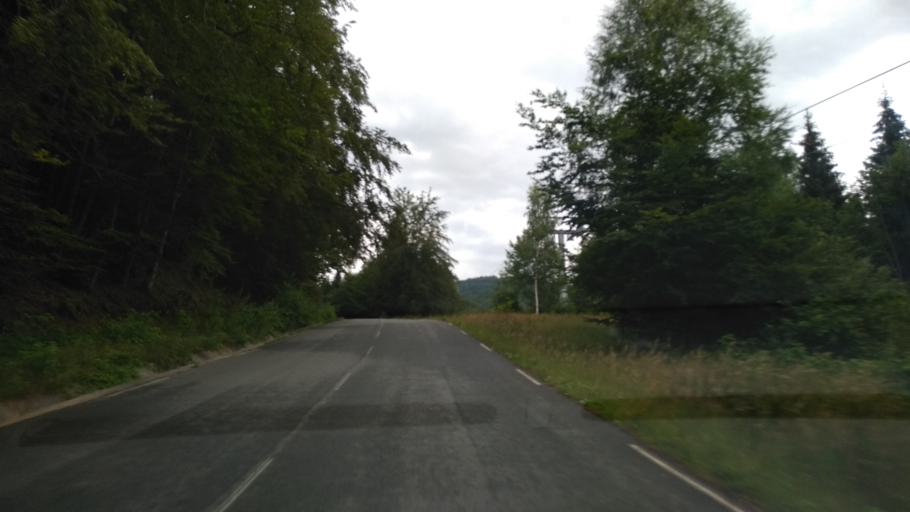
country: RO
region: Hunedoara
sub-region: Municipiul  Vulcan
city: Jiu-Paroseni
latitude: 45.3446
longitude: 23.2907
